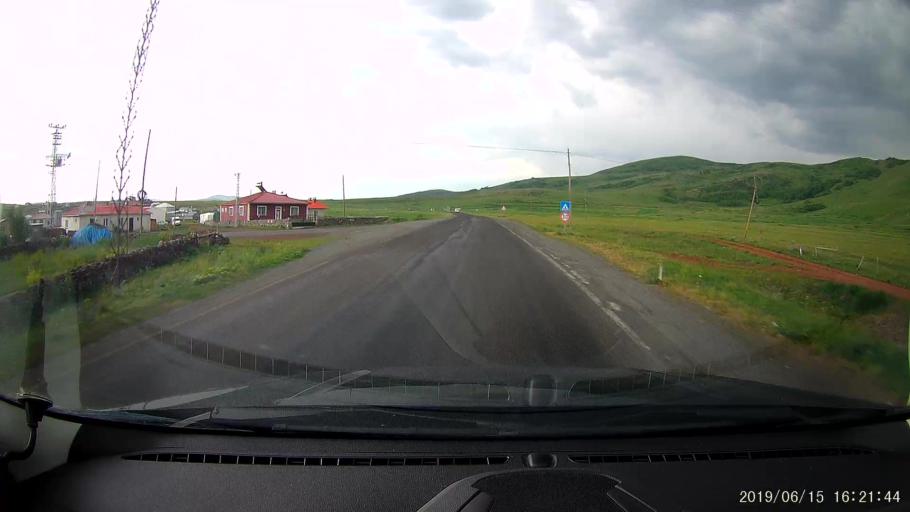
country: TR
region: Ardahan
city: Hanak
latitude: 41.1957
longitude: 42.8456
